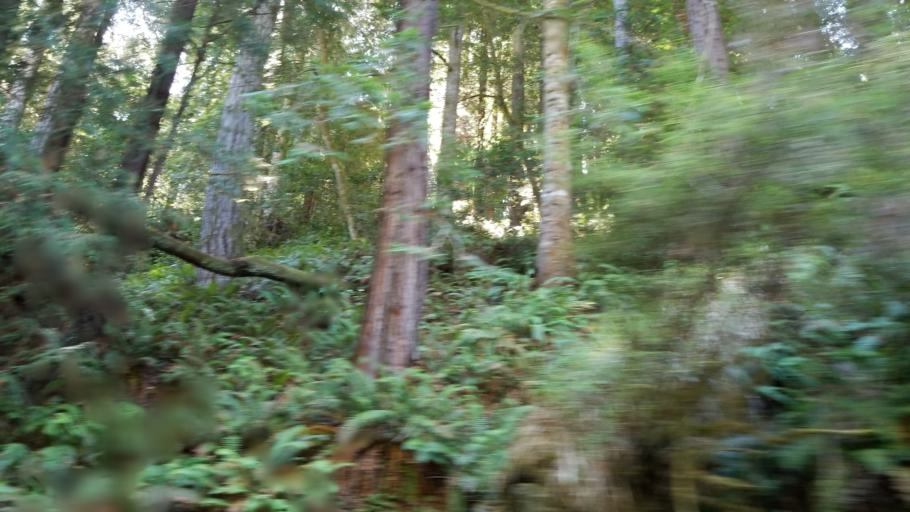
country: US
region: California
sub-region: Mendocino County
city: Fort Bragg
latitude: 39.4477
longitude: -123.7723
